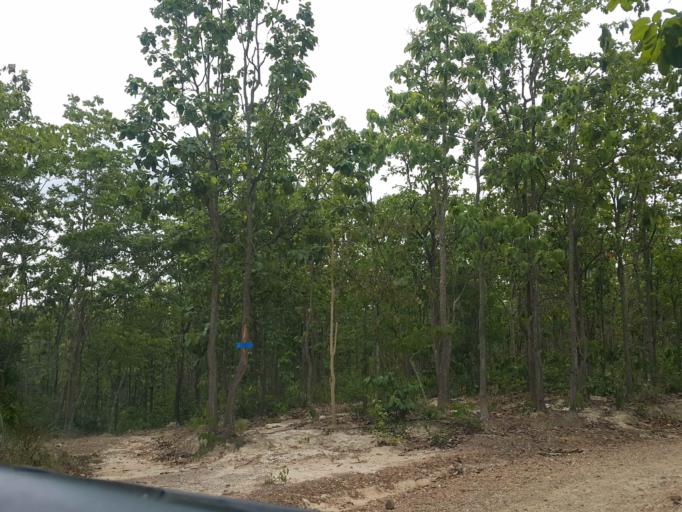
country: TH
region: Chiang Mai
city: Doi Lo
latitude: 18.5096
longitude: 98.7414
